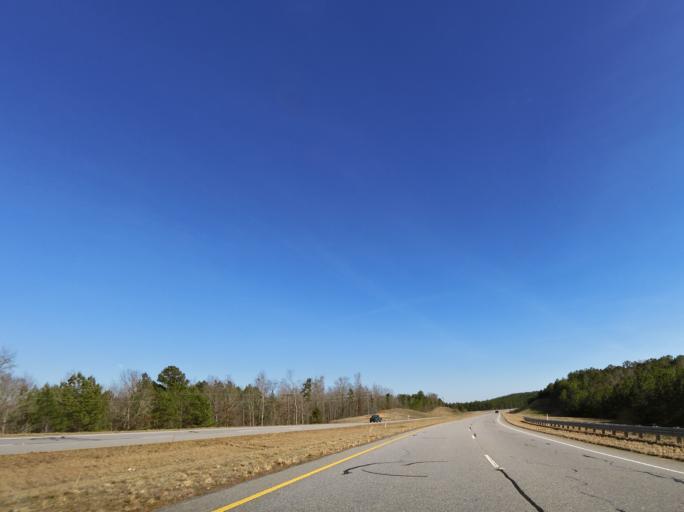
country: US
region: Georgia
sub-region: Upson County
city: Thomaston
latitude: 32.7440
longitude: -84.2259
